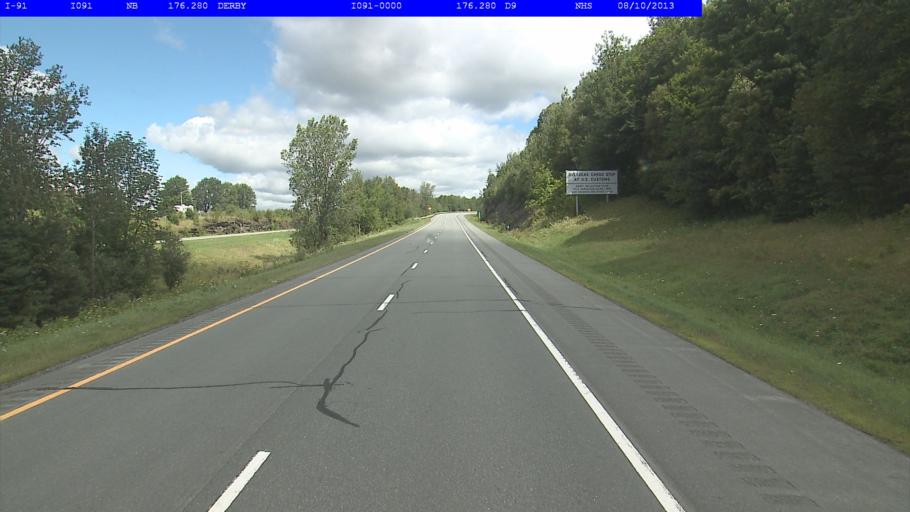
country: US
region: Vermont
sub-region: Orleans County
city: Newport
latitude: 44.9937
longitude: -72.1019
